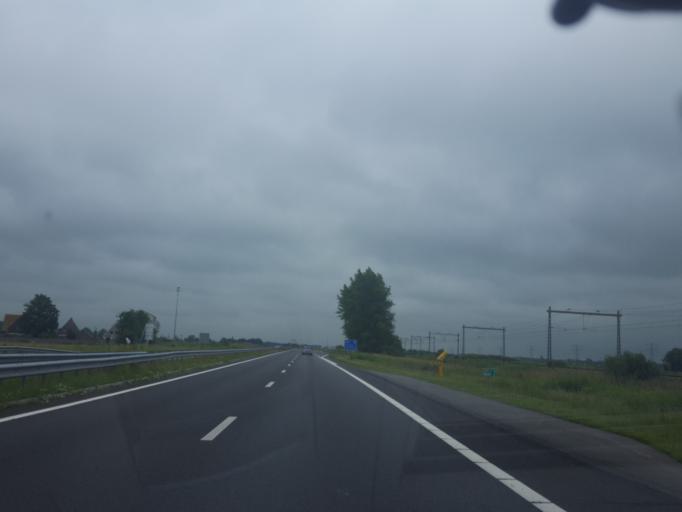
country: NL
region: Friesland
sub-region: Gemeente Leeuwarden
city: Wirdum
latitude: 53.1492
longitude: 5.7935
